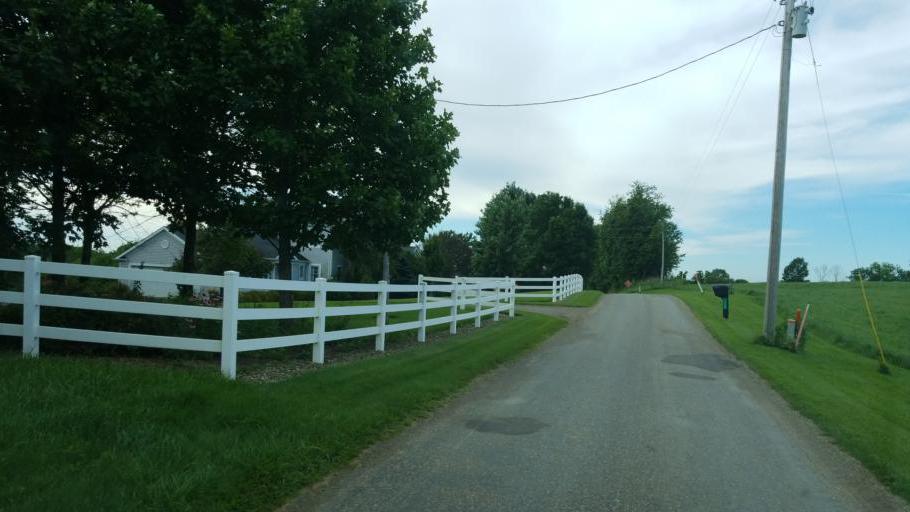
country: US
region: Ohio
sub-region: Holmes County
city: Millersburg
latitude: 40.5010
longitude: -81.8489
